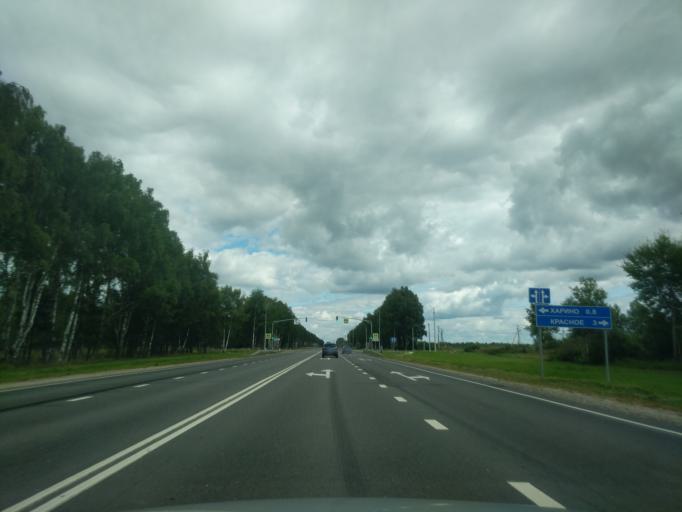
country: RU
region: Jaroslavl
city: Nekrasovskoye
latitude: 57.6078
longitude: 40.3309
